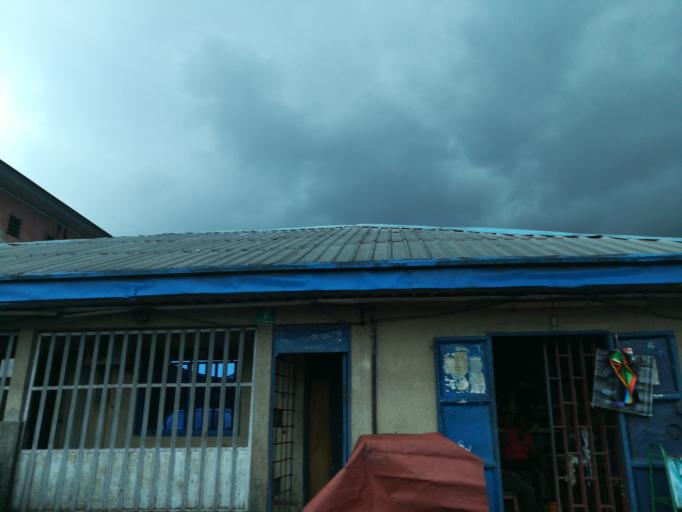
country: NG
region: Rivers
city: Port Harcourt
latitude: 4.8018
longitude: 6.9896
